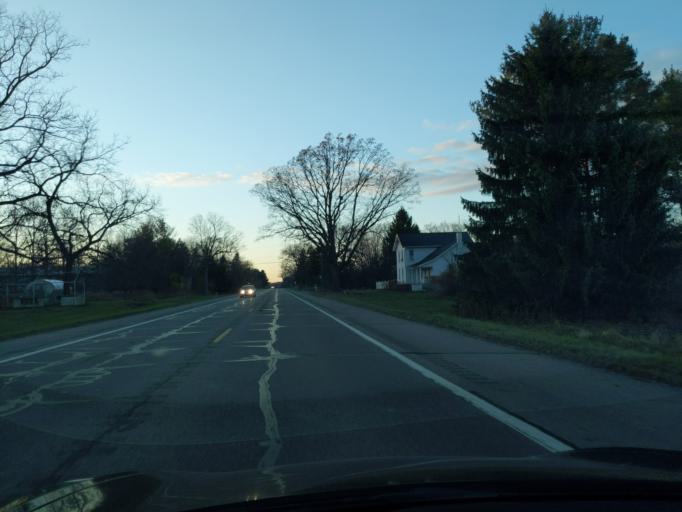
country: US
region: Michigan
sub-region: Ingham County
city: Haslett
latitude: 42.7057
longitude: -84.3522
